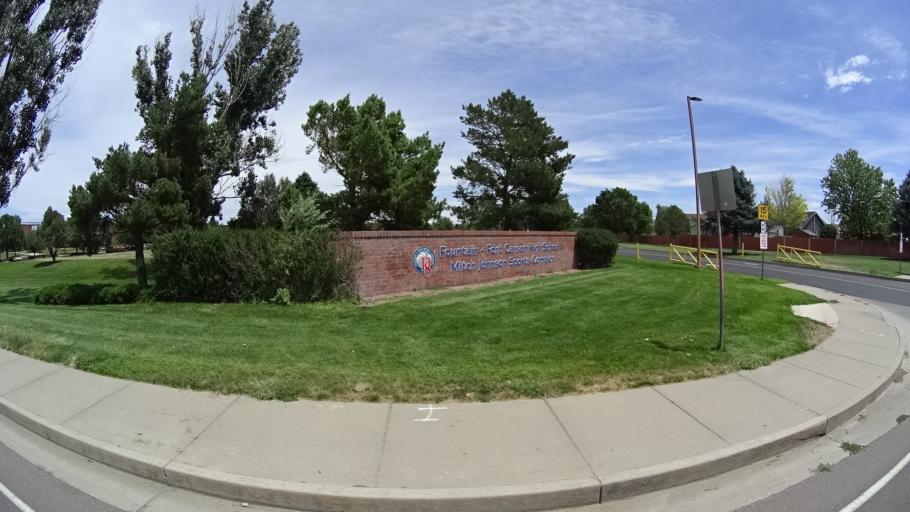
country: US
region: Colorado
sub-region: El Paso County
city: Fountain
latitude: 38.6710
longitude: -104.6834
